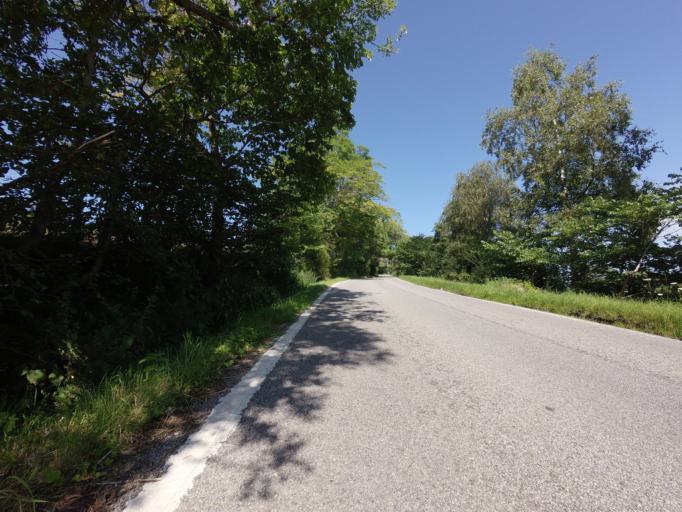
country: GB
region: Scotland
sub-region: Highland
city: Dingwall
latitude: 57.6126
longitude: -4.4146
